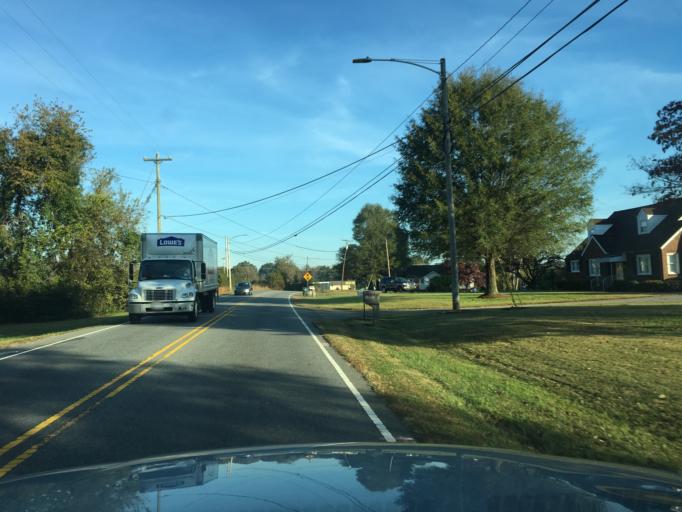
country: US
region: North Carolina
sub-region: Catawba County
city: Newton
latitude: 35.6423
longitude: -81.2692
